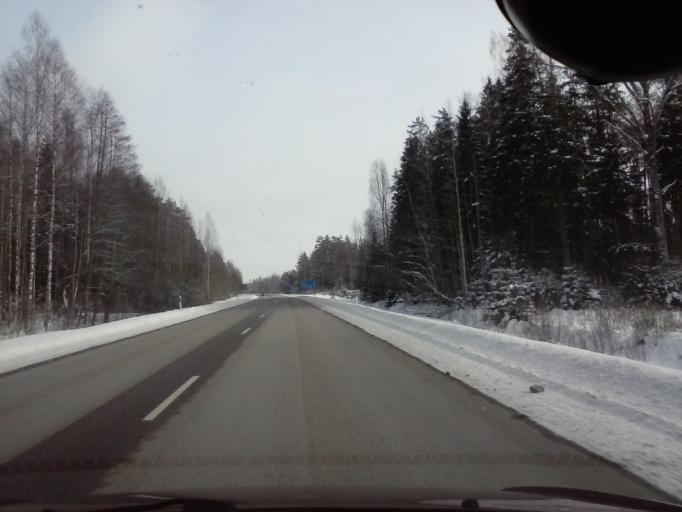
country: EE
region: Paernumaa
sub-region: Saarde vald
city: Kilingi-Nomme
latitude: 58.1634
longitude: 24.8374
